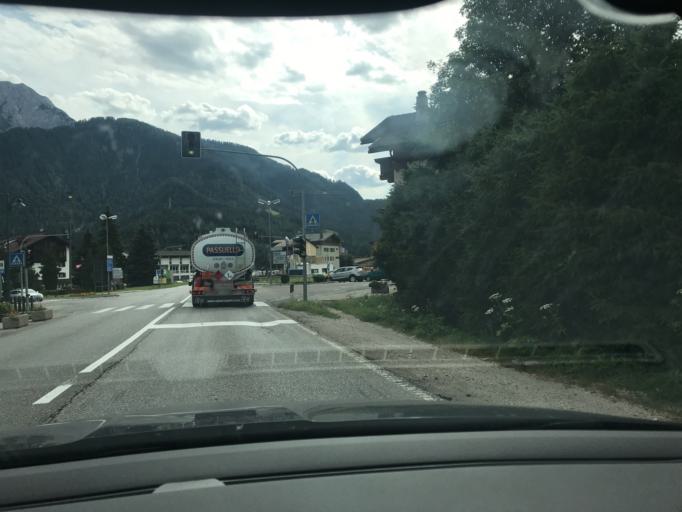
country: IT
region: Trentino-Alto Adige
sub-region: Bolzano
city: Dobbiaco
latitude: 46.7298
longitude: 12.2244
